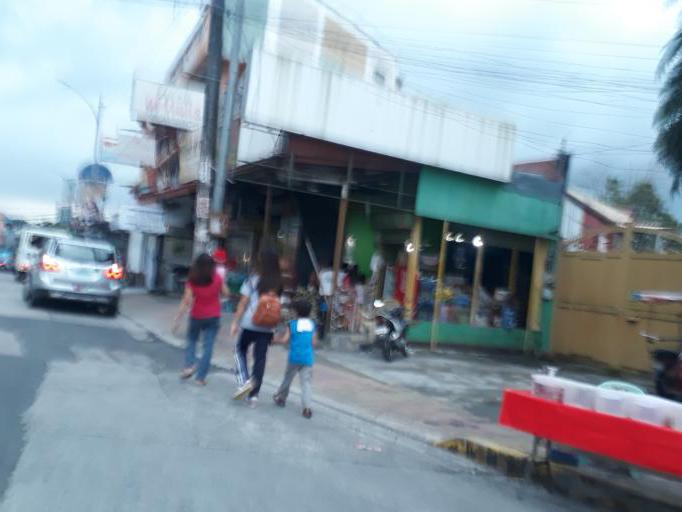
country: PH
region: Metro Manila
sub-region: Quezon City
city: Quezon City
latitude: 14.6827
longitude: 121.0796
